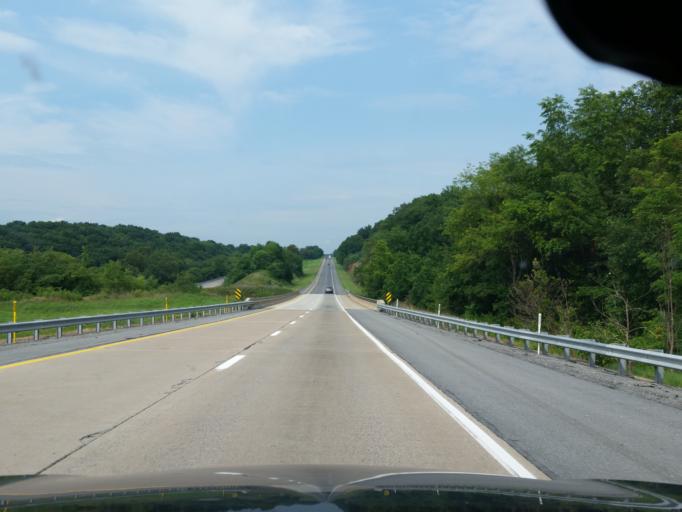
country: US
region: Pennsylvania
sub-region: Juniata County
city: Mifflintown
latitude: 40.5608
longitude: -77.2728
